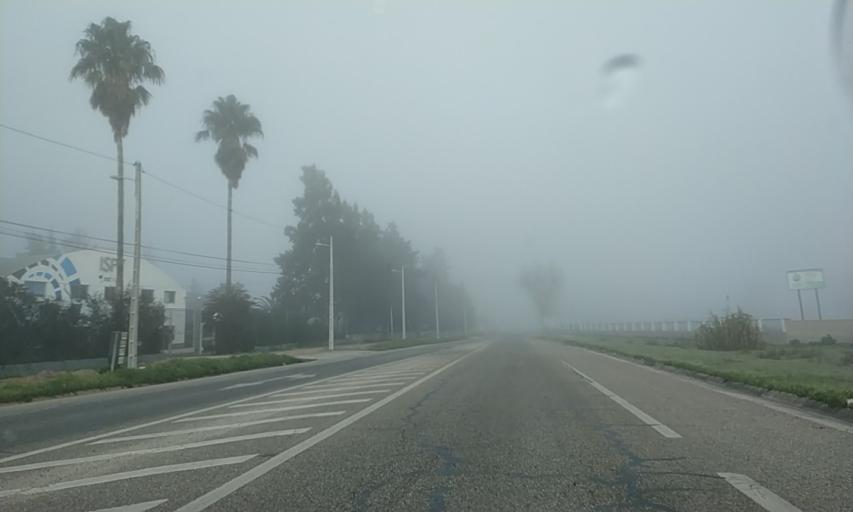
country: PT
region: Setubal
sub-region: Palmela
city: Pinhal Novo
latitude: 38.6526
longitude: -8.9175
